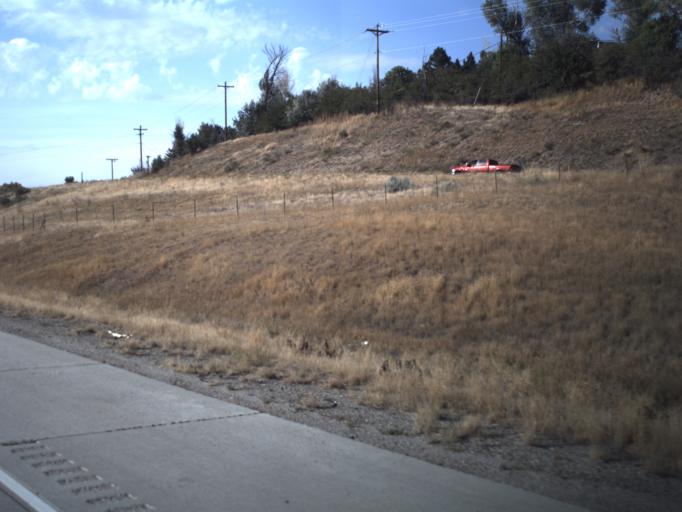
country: US
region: Utah
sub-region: Morgan County
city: Morgan
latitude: 41.0653
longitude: -111.7099
